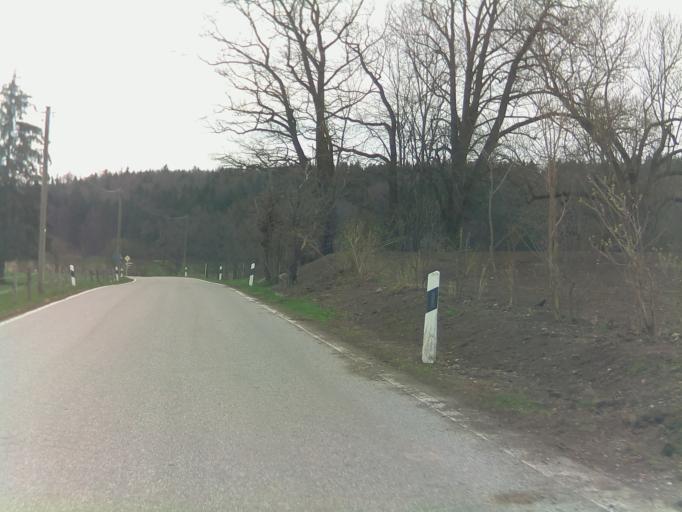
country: DE
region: Bavaria
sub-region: Upper Bavaria
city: Obersochering
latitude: 47.7608
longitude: 11.2289
